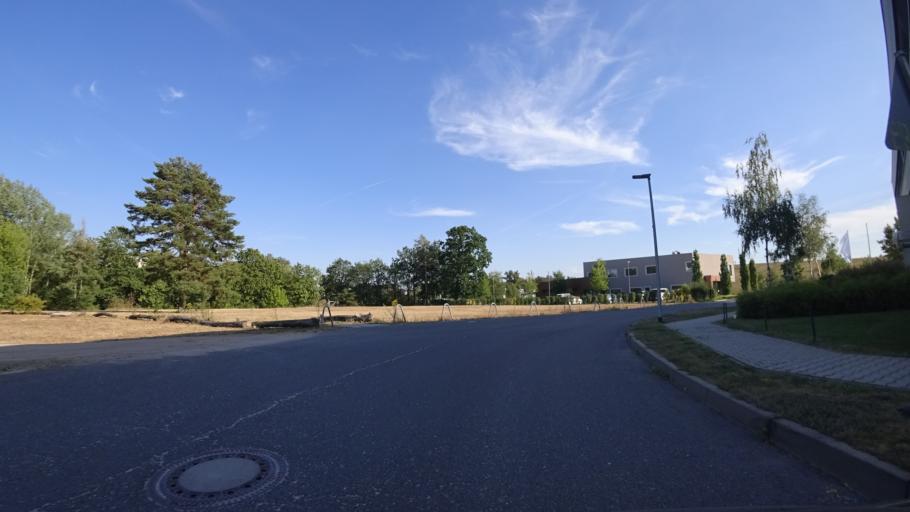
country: DE
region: Brandenburg
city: Stahnsdorf
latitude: 52.4034
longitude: 13.1959
